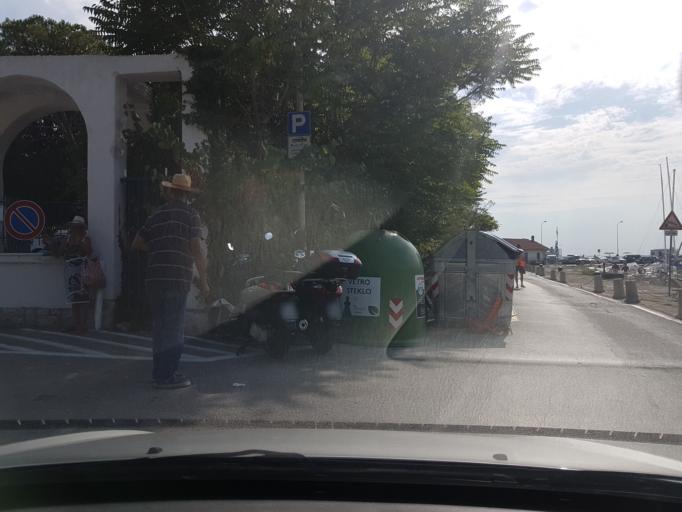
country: IT
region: Friuli Venezia Giulia
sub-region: Provincia di Trieste
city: Sistiana-Visogliano
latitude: 45.7684
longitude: 13.6323
